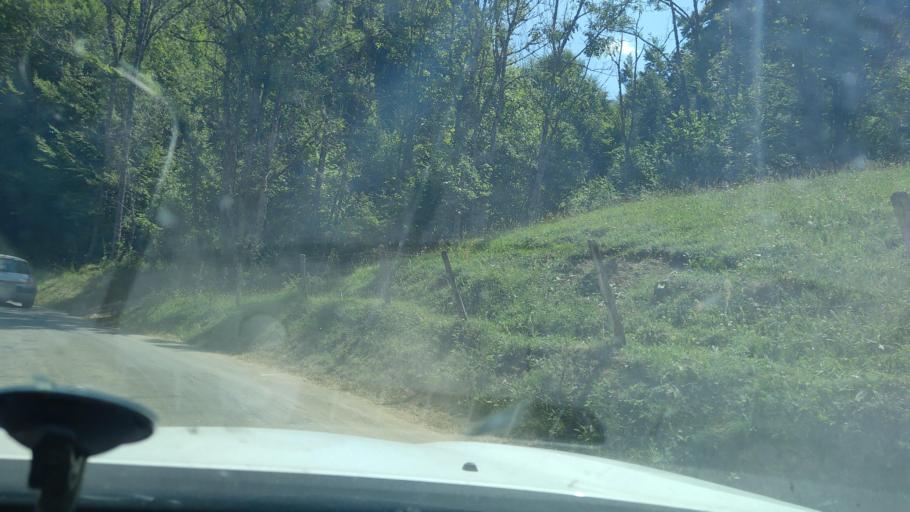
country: FR
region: Rhone-Alpes
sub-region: Departement de la Savoie
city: Mery
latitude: 45.6619
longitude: 6.0330
